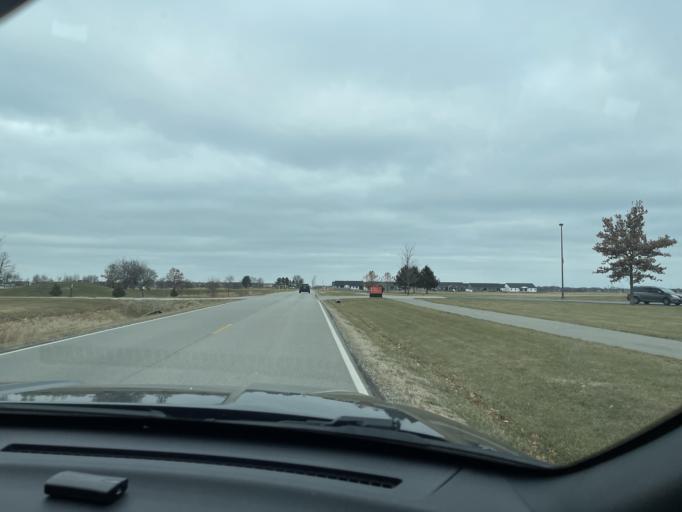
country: US
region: Illinois
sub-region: Sangamon County
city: Jerome
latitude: 39.7582
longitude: -89.7532
